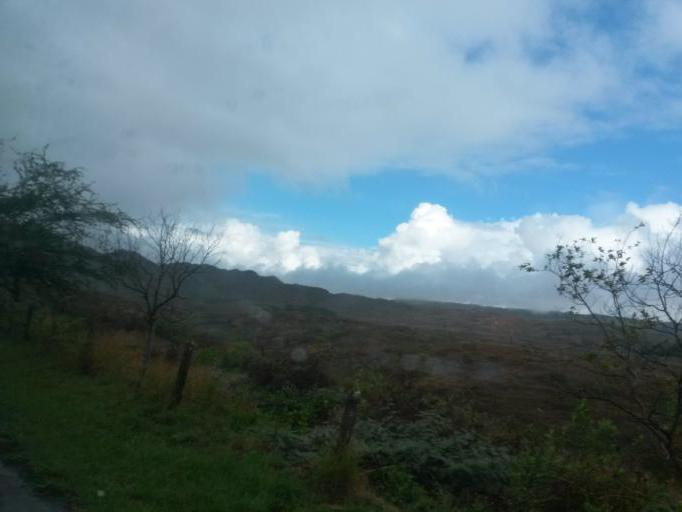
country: CO
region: Cauca
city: El Bordo
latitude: 2.1468
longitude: -76.9278
